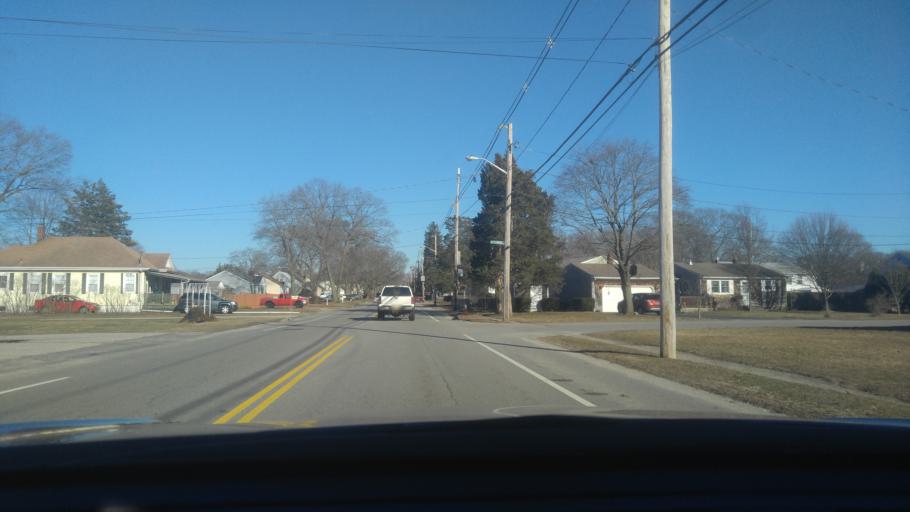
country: US
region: Rhode Island
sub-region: Kent County
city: Warwick
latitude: 41.6973
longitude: -71.4381
